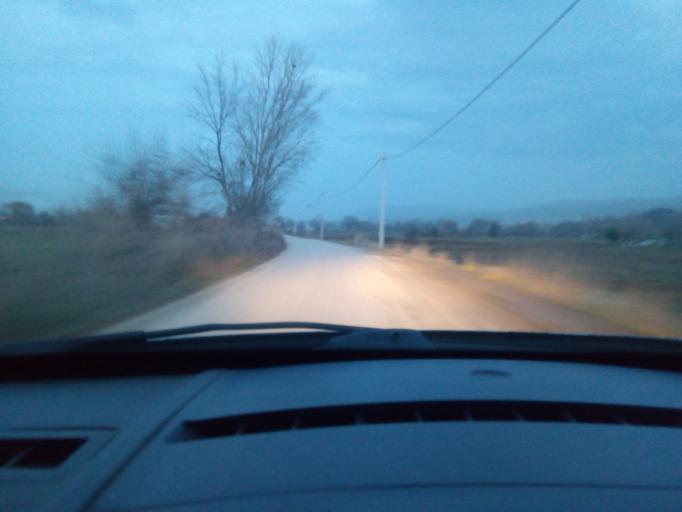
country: TR
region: Balikesir
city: Susurluk
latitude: 39.9195
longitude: 28.1355
